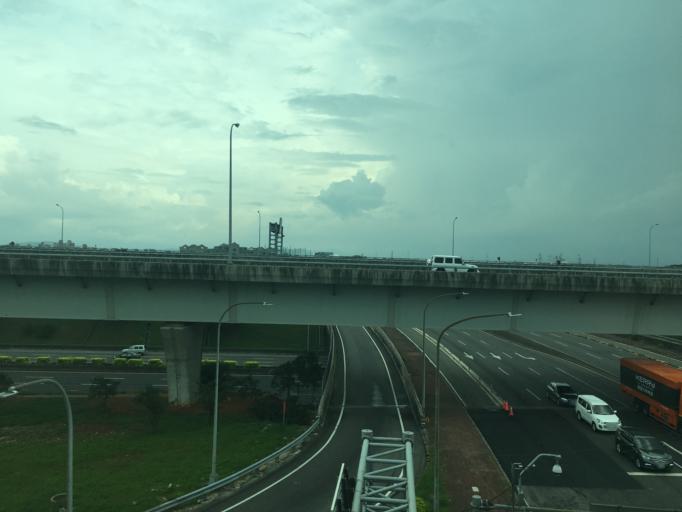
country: TW
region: Taiwan
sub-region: Taoyuan
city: Taoyuan
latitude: 25.0660
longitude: 121.3554
